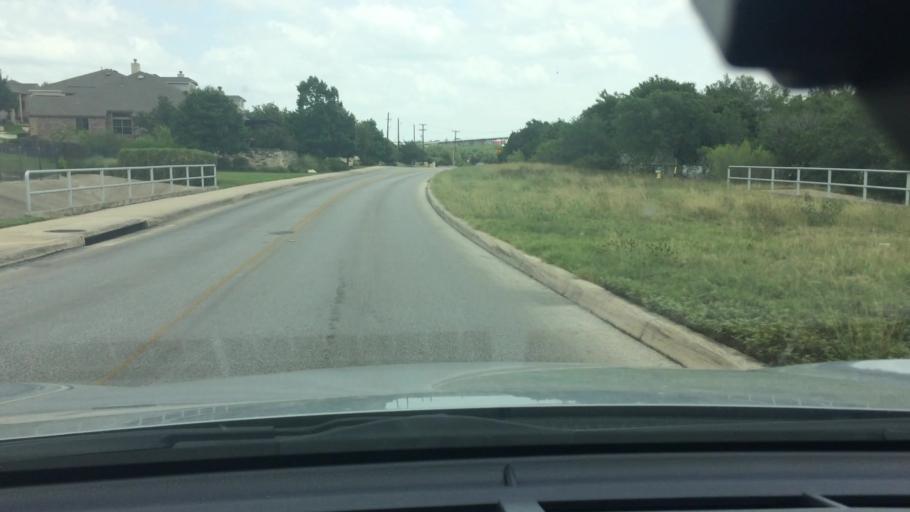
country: US
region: Texas
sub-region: Bexar County
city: Timberwood Park
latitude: 29.6624
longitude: -98.5068
